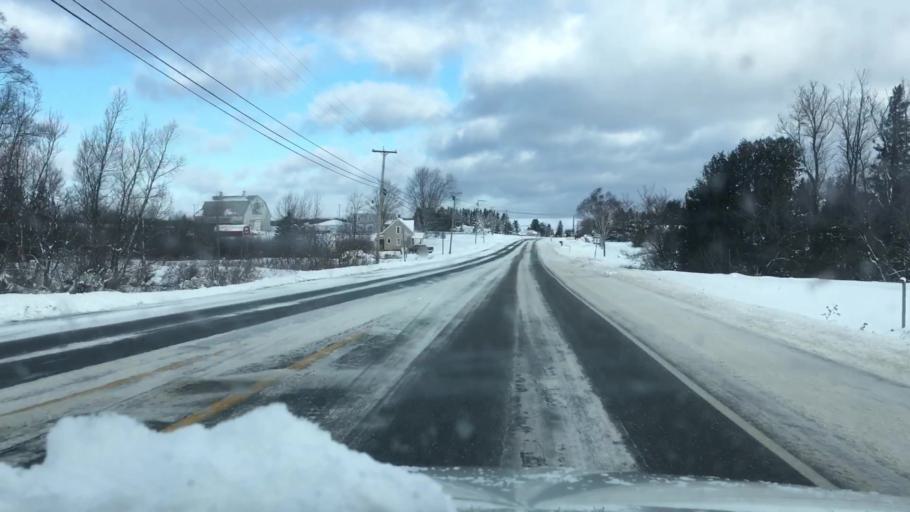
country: US
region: Maine
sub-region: Aroostook County
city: Caribou
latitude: 46.8886
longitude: -68.0144
